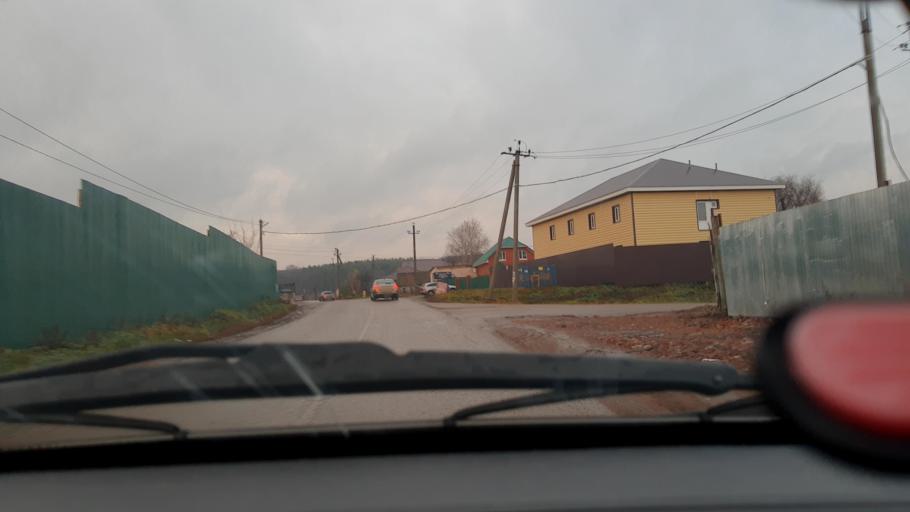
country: RU
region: Bashkortostan
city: Mikhaylovka
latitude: 54.8021
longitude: 55.8804
